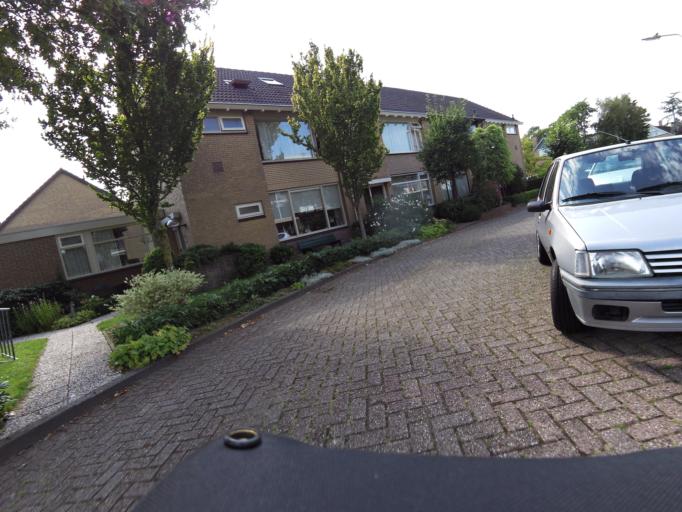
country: NL
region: South Holland
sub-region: Gemeente Oud-Beijerland
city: Oud-Beijerland
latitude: 51.8170
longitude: 4.4247
